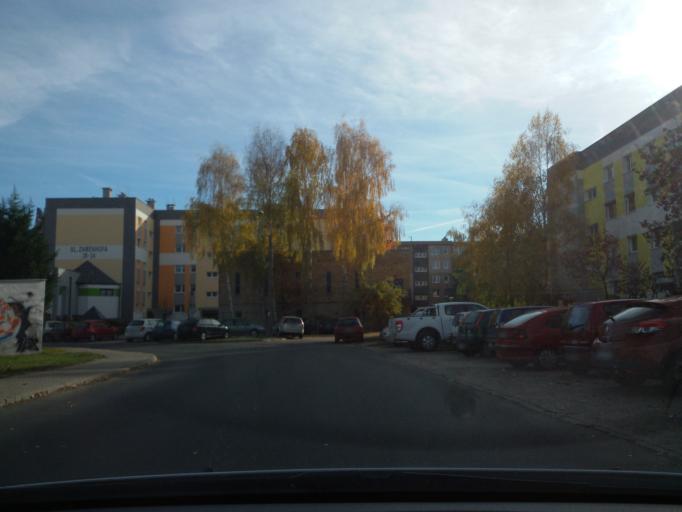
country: PL
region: Greater Poland Voivodeship
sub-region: Leszno
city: Leszno
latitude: 51.8355
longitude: 16.5989
